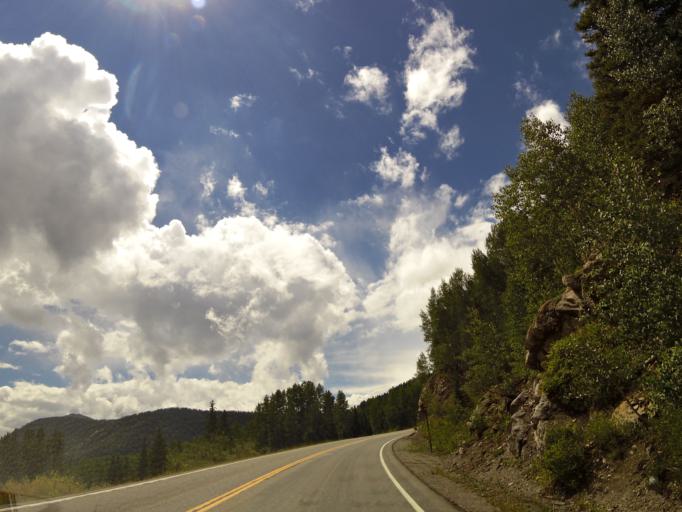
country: US
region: Colorado
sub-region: San Juan County
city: Silverton
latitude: 37.7130
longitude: -107.7563
